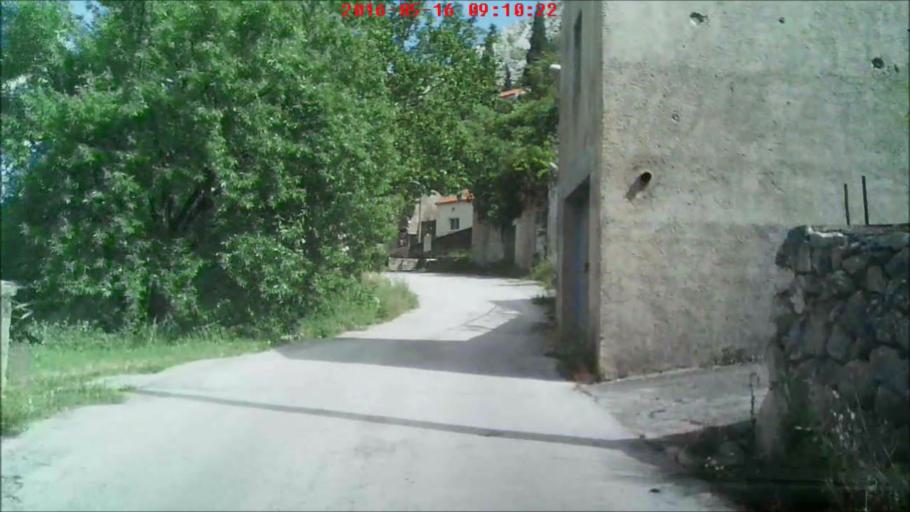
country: HR
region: Dubrovacko-Neretvanska
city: Podgora
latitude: 42.8178
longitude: 17.8565
